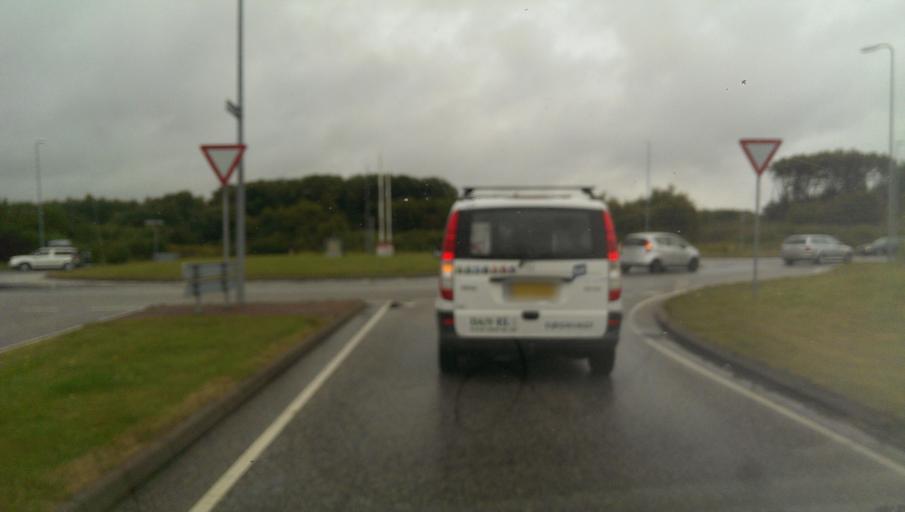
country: DK
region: South Denmark
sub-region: Esbjerg Kommune
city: Esbjerg
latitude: 55.5175
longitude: 8.4685
